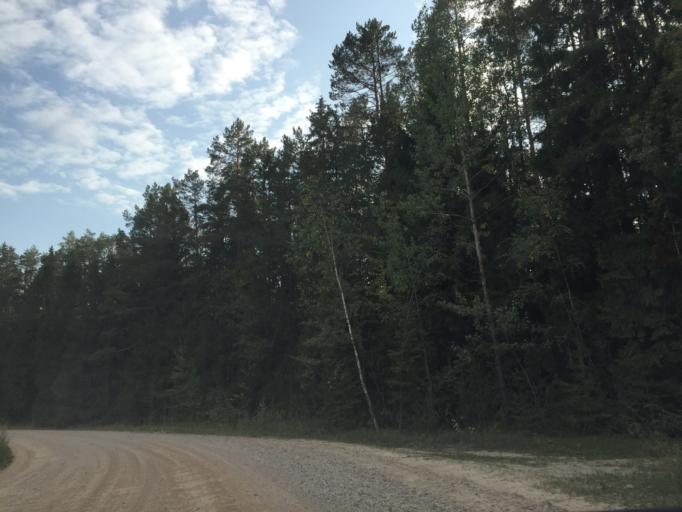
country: LV
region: Ikskile
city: Ikskile
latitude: 56.8002
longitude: 24.4373
